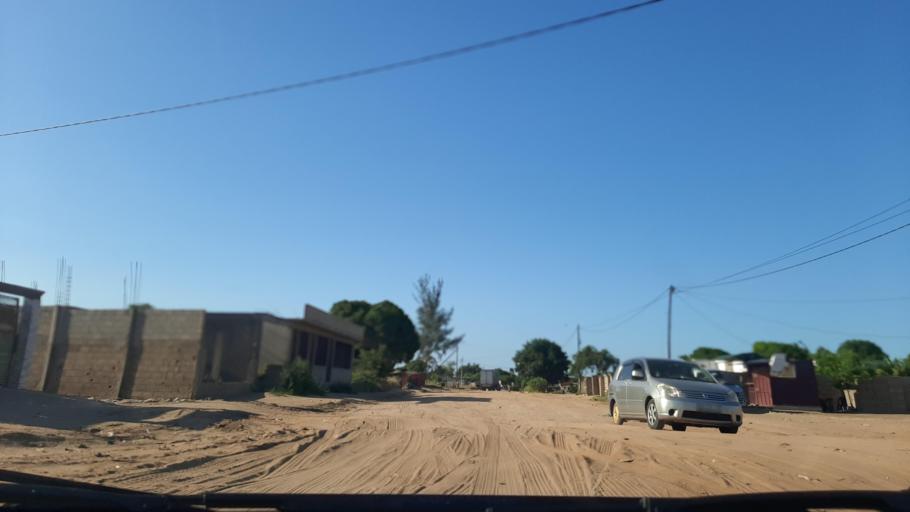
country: MZ
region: Maputo City
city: Maputo
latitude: -25.8048
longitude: 32.5469
